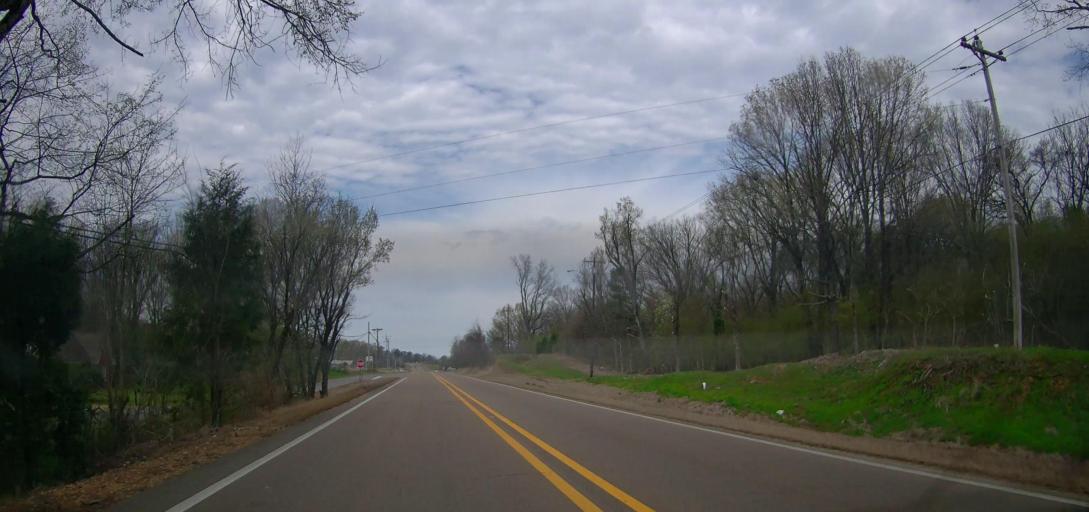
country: US
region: Mississippi
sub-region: De Soto County
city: Olive Branch
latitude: 34.9723
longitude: -89.8405
